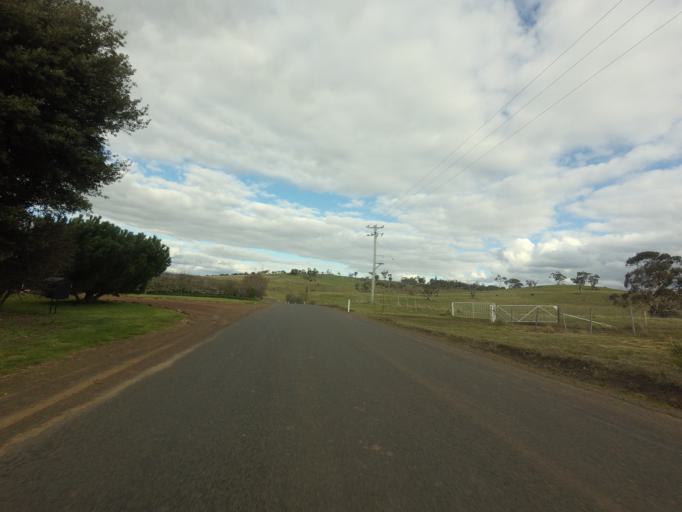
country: AU
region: Tasmania
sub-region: Northern Midlands
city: Evandale
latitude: -41.8869
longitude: 147.3155
